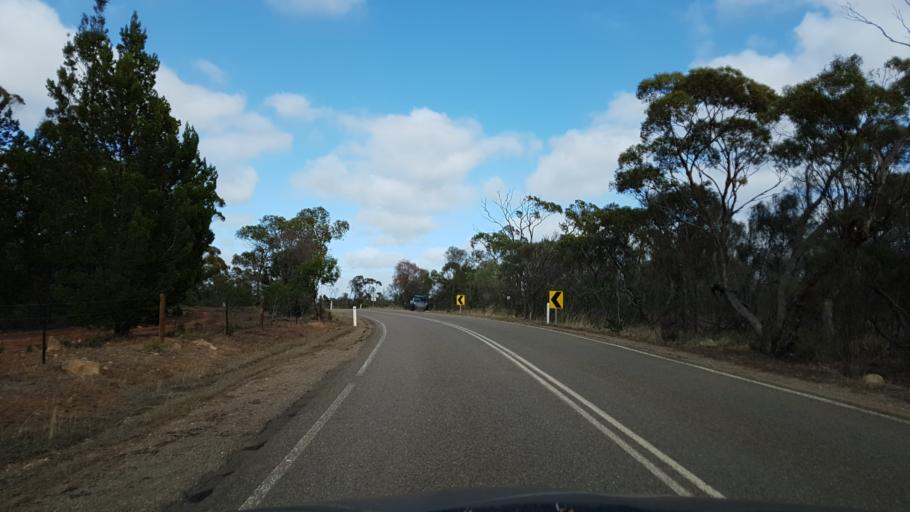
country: AU
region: South Australia
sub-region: Murray Bridge
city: Murray Bridge
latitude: -35.1122
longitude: 139.2226
